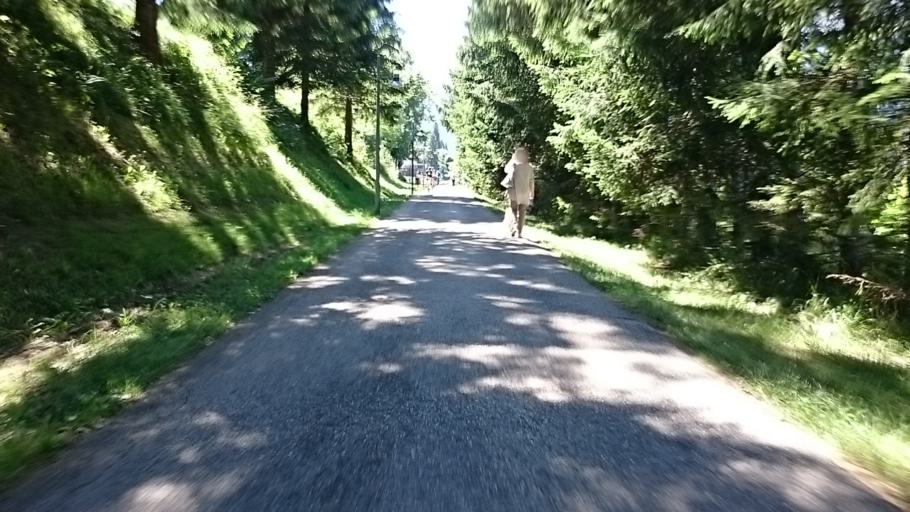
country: IT
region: Veneto
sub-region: Provincia di Belluno
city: Cortina d'Ampezzo
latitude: 46.5295
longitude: 12.1415
